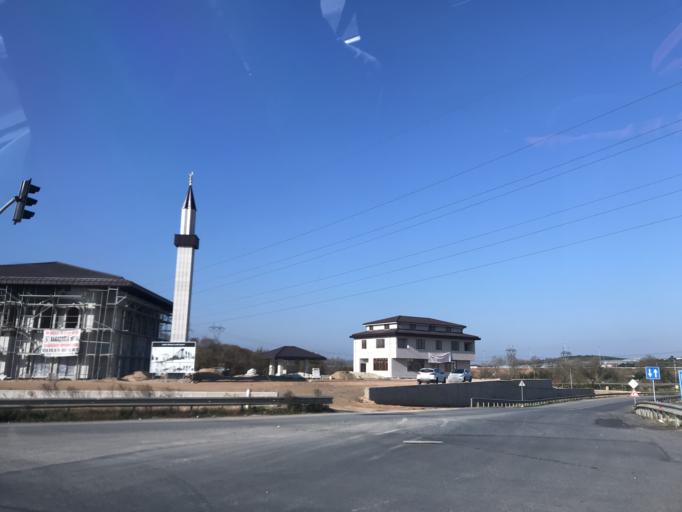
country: TR
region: Istanbul
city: Sultanbeyli
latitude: 40.9346
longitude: 29.3568
